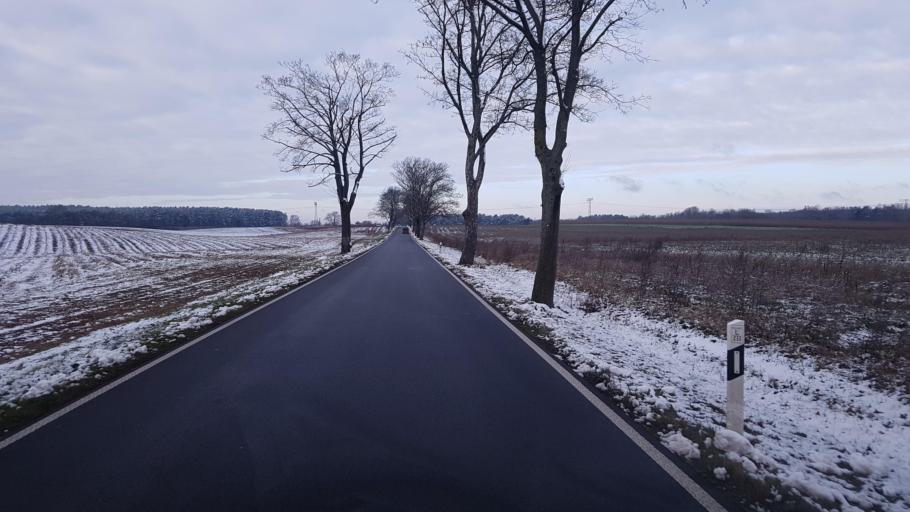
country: DE
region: Brandenburg
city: Strausberg
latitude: 52.5594
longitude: 13.9073
